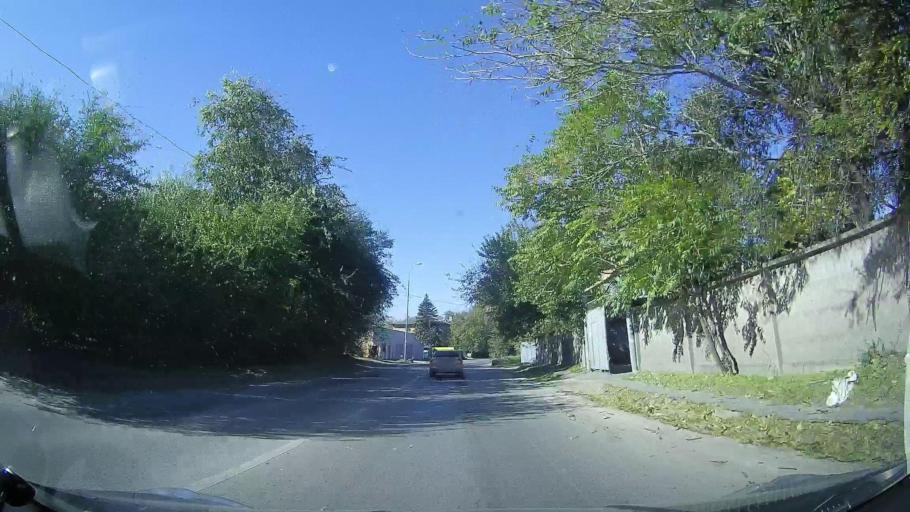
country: RU
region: Rostov
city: Rostov-na-Donu
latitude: 47.2266
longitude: 39.6733
